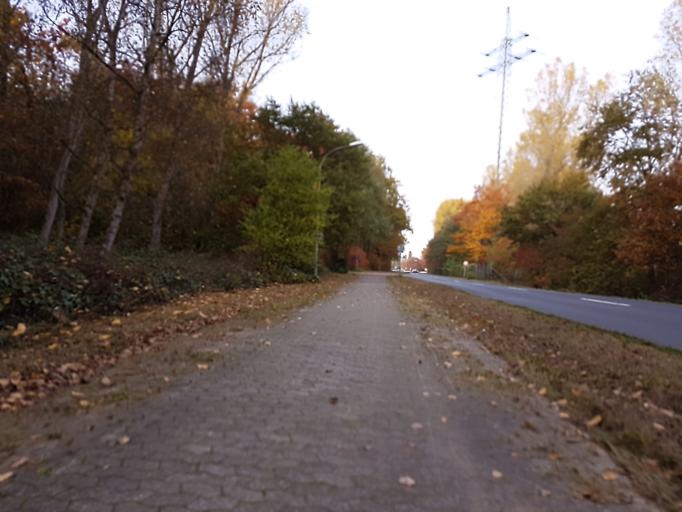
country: DE
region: Bavaria
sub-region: Regierungsbezirk Unterfranken
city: Obernburg am Main
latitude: 49.8215
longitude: 9.1454
